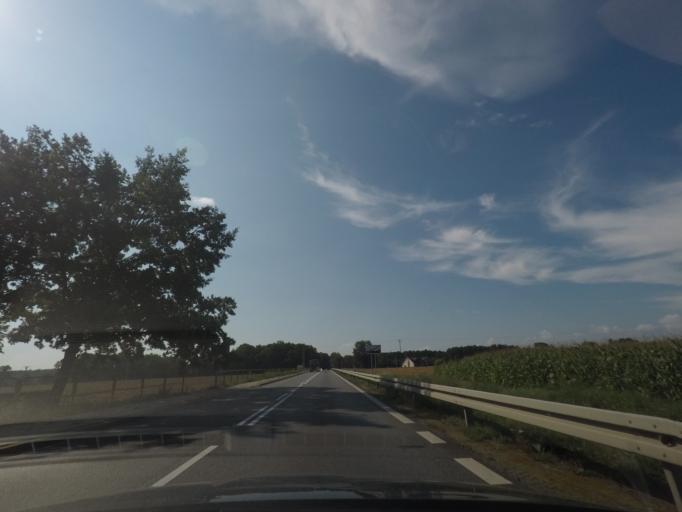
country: PL
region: Silesian Voivodeship
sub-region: Powiat pszczynski
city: Radostowice
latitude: 50.0138
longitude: 18.8553
